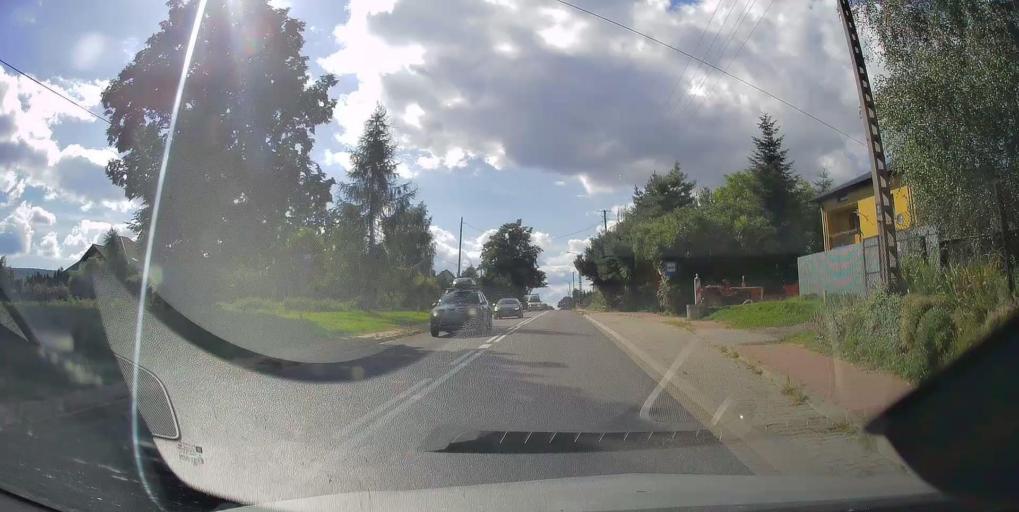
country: PL
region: Swietokrzyskie
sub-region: Powiat kielecki
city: Nowa Slupia
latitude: 50.8829
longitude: 21.0520
